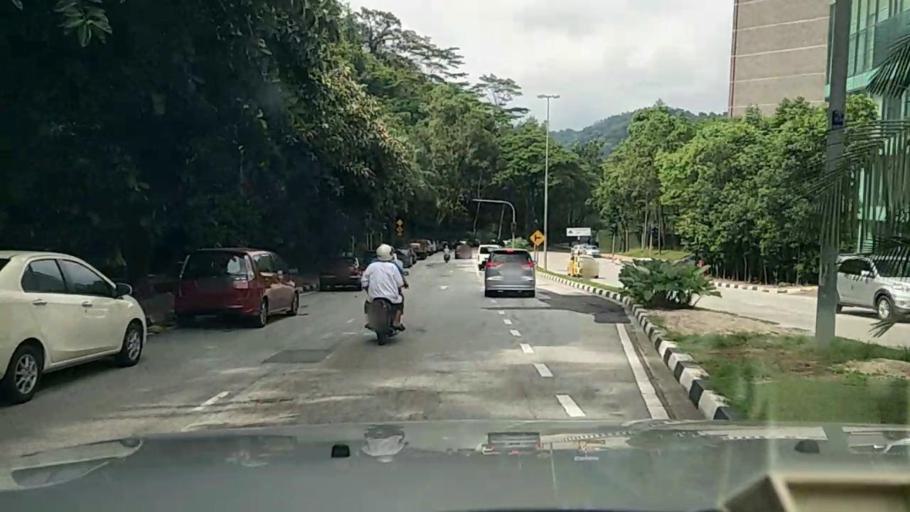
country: MY
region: Selangor
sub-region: Petaling
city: Petaling Jaya
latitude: 3.1677
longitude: 101.6120
